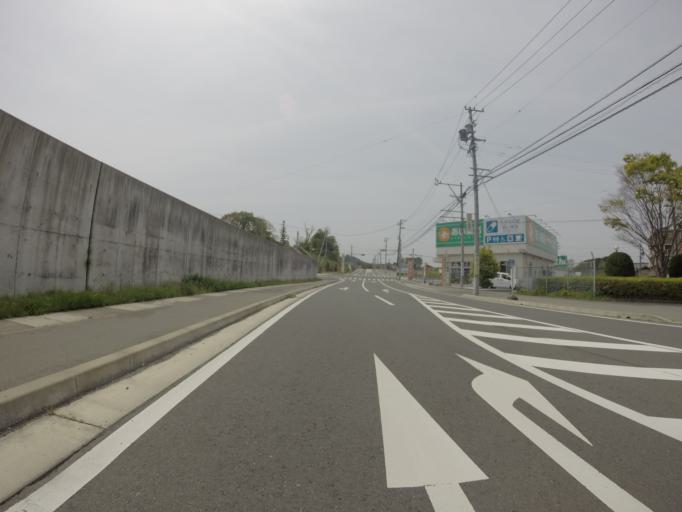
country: JP
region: Shizuoka
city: Kakegawa
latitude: 34.7589
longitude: 137.9973
